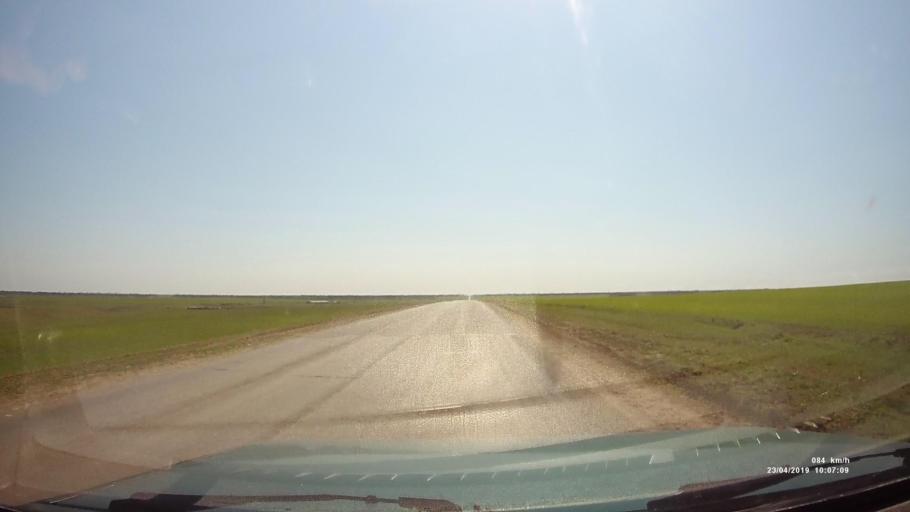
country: RU
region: Rostov
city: Sovetskoye
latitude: 46.7272
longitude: 42.2490
